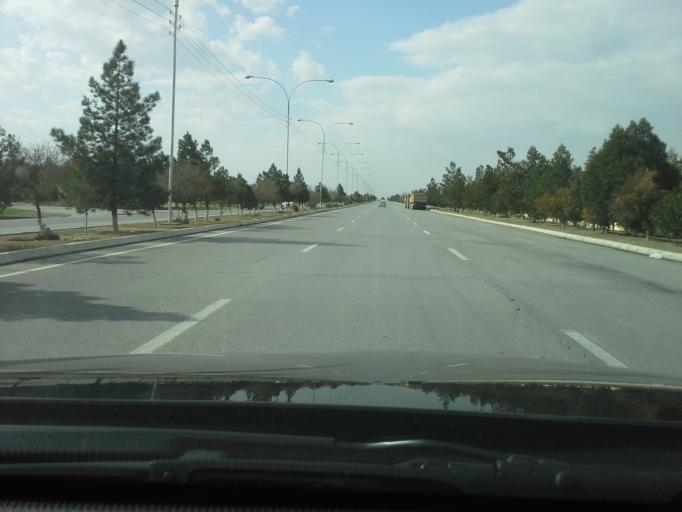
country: TM
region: Ahal
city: Ashgabat
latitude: 37.9657
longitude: 58.3059
